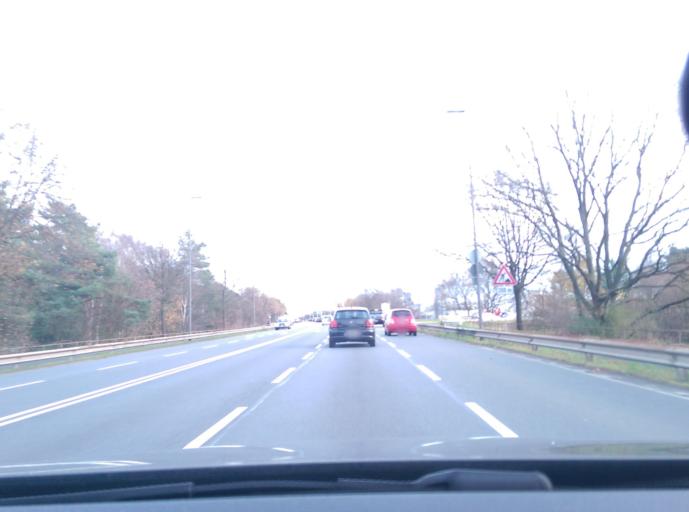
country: DE
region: Lower Saxony
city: Celle
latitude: 52.6077
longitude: 10.0521
